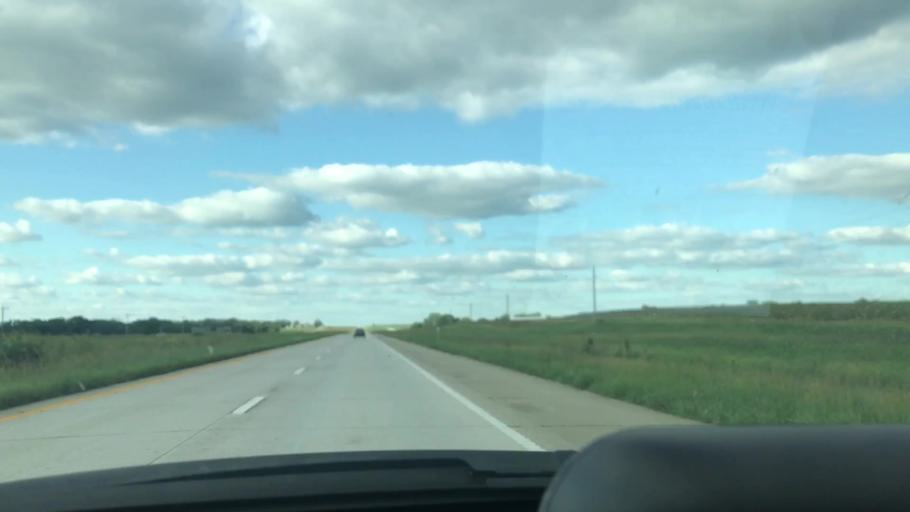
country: US
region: Missouri
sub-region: Benton County
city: Cole Camp
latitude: 38.4891
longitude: -93.2737
